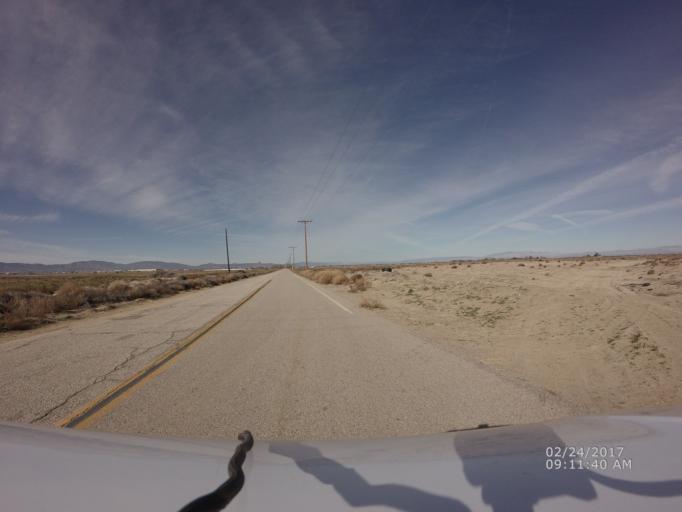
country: US
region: California
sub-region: Los Angeles County
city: Lancaster
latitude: 34.6607
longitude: -118.0233
